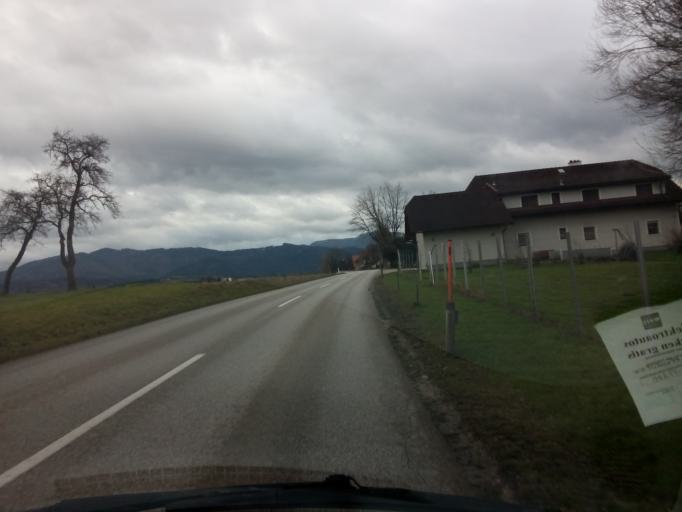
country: AT
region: Upper Austria
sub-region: Politischer Bezirk Gmunden
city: Scharnstein
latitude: 47.9740
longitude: 14.0186
